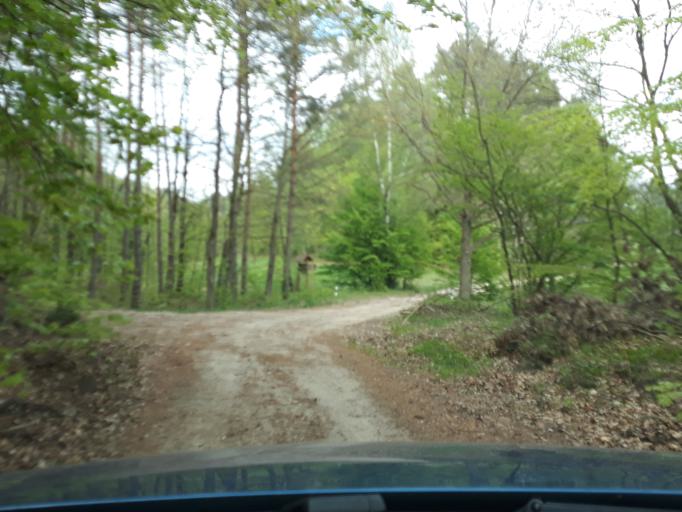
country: PL
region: Pomeranian Voivodeship
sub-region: Powiat czluchowski
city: Czluchow
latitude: 53.7551
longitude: 17.3573
